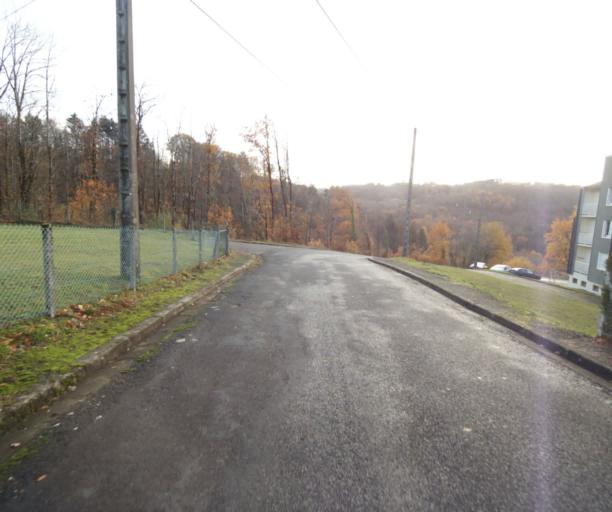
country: FR
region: Limousin
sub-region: Departement de la Correze
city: Cornil
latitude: 45.2069
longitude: 1.6960
